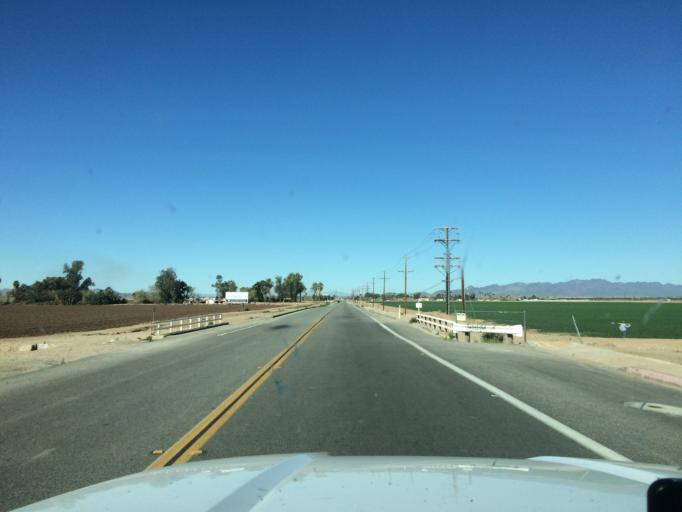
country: US
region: California
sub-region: Riverside County
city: Blythe
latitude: 33.6102
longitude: -114.6138
